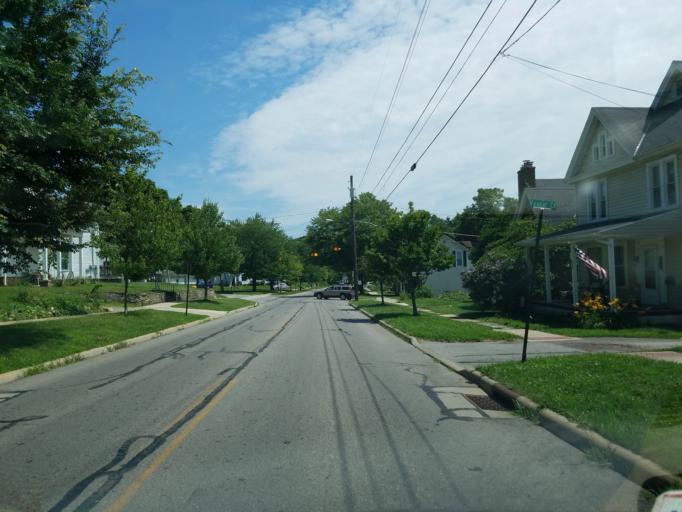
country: US
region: Ohio
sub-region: Ashland County
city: Ashland
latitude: 40.8718
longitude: -82.3227
